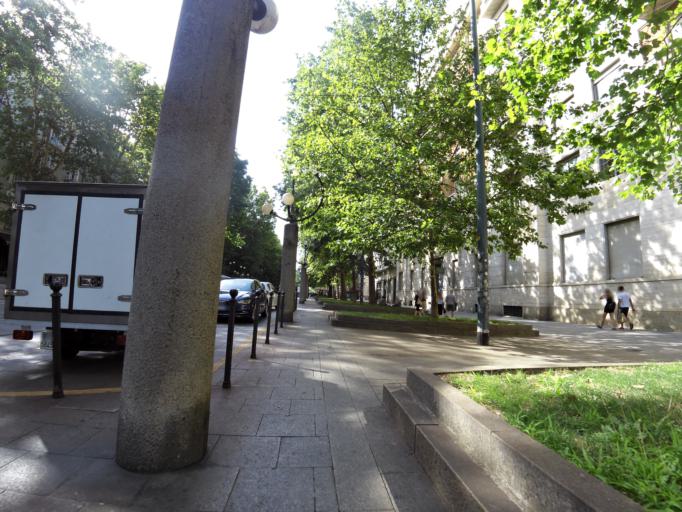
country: IT
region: Lombardy
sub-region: Citta metropolitana di Milano
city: Milano
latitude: 45.4766
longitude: 9.1714
